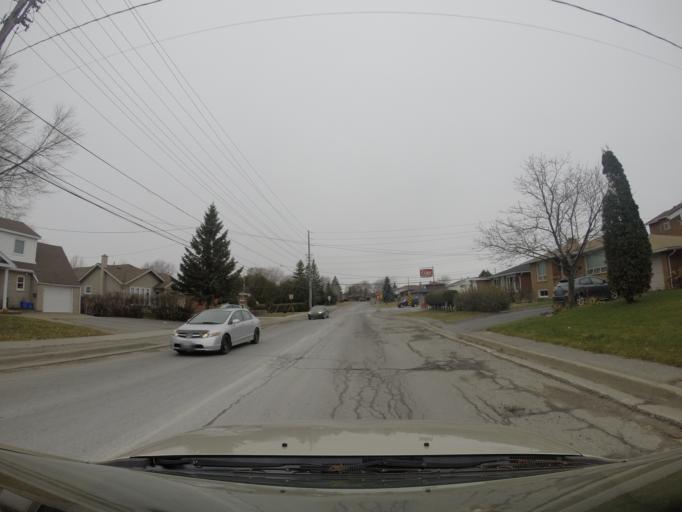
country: CA
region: Ontario
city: Greater Sudbury
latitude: 46.4602
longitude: -81.0272
